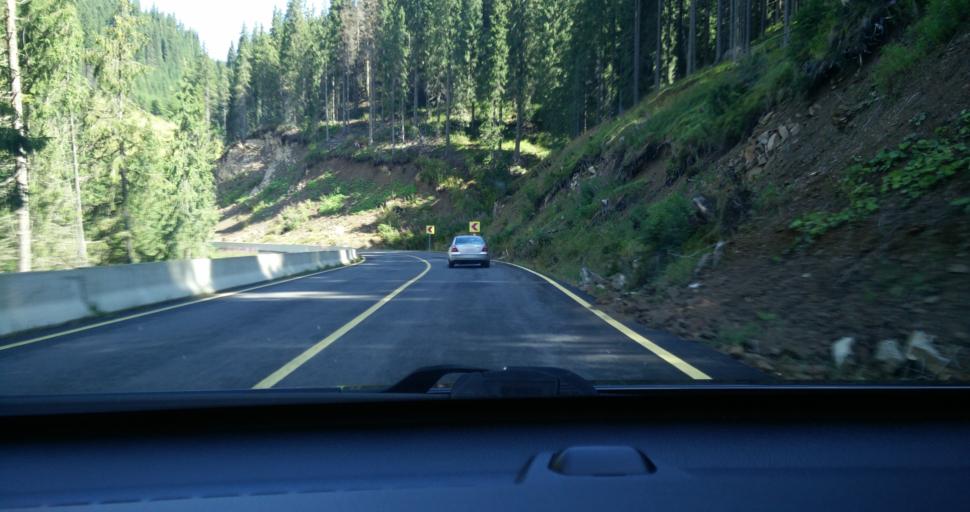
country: RO
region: Hunedoara
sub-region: Oras Petrila
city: Petrila
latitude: 45.4441
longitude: 23.6246
